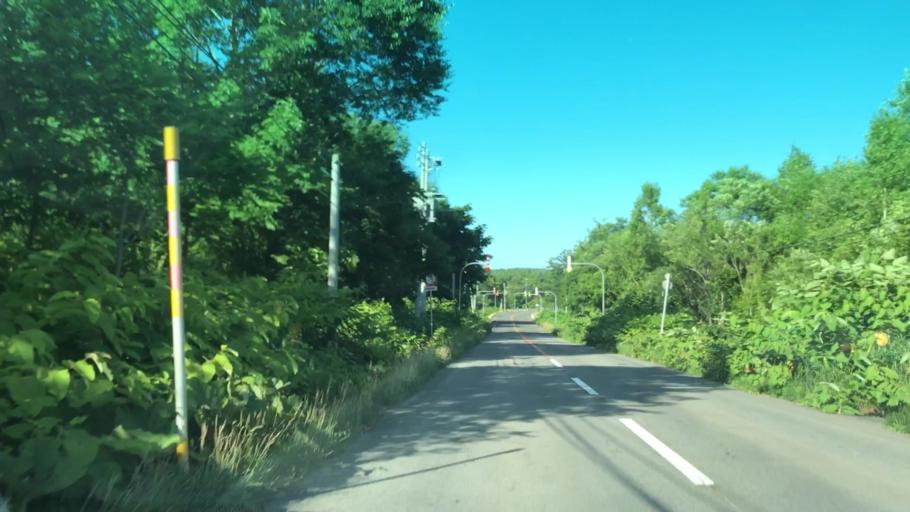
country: JP
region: Hokkaido
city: Yoichi
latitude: 43.0591
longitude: 140.8681
